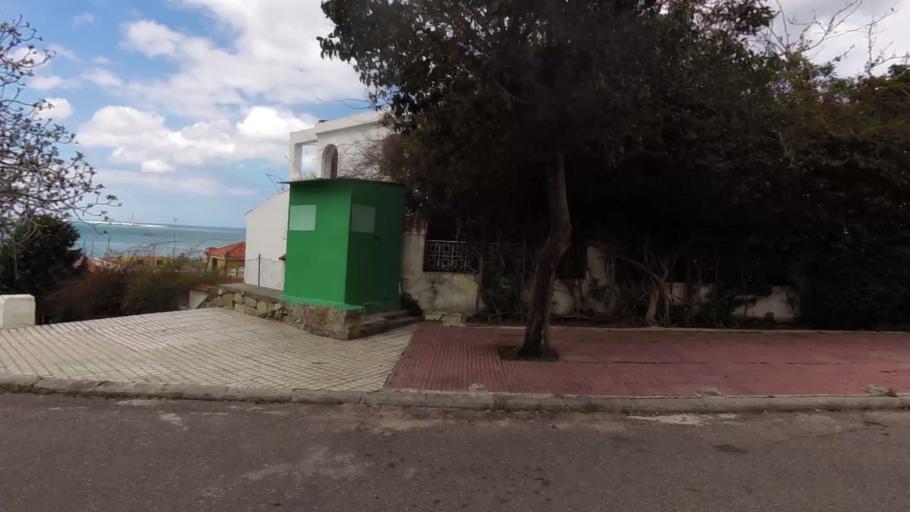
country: MA
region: Tanger-Tetouan
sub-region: Tanger-Assilah
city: Tangier
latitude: 35.7774
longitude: -5.7740
